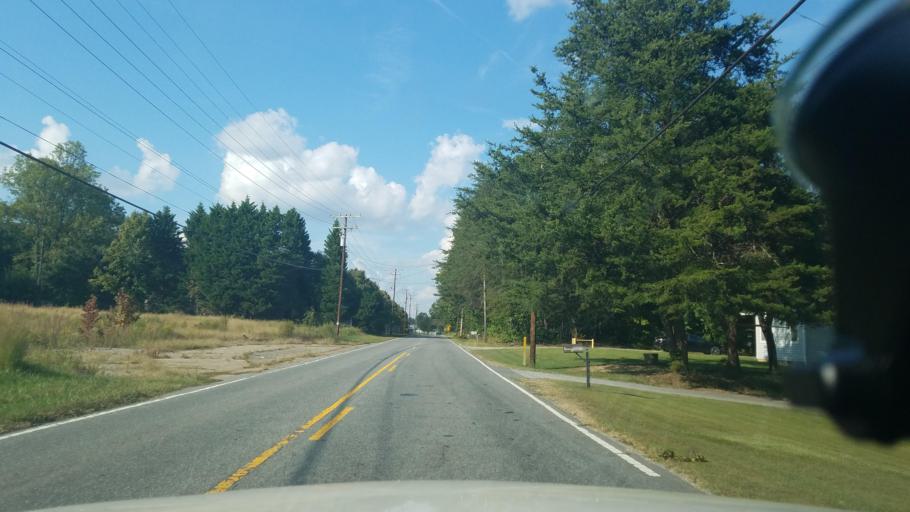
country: US
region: North Carolina
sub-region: Guilford County
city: Greensboro
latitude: 36.0181
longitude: -79.7762
